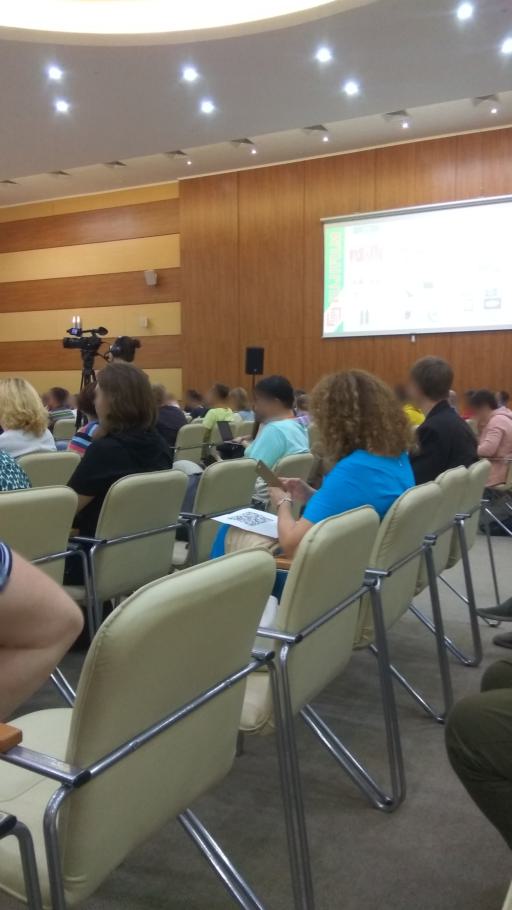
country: RU
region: Primorskiy
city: Russkiy
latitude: 43.0247
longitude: 131.8923
